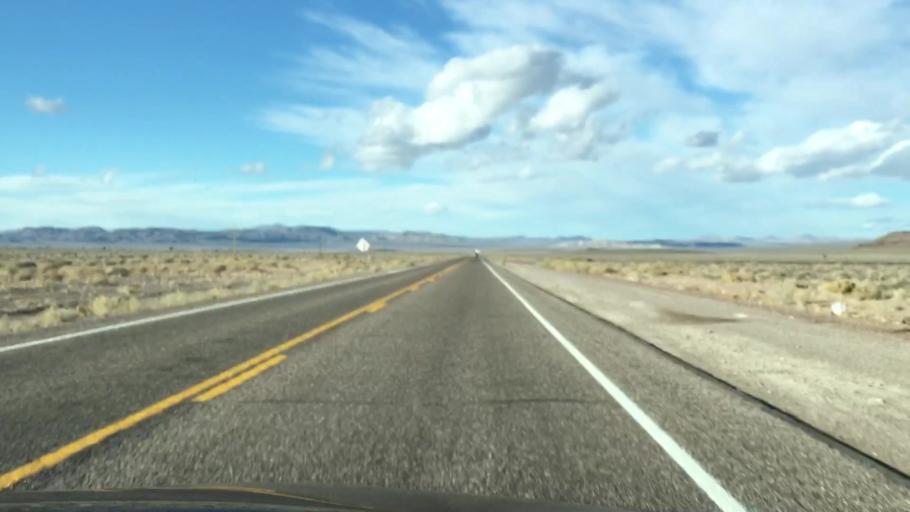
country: US
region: Nevada
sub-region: Esmeralda County
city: Goldfield
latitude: 37.3917
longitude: -117.1452
